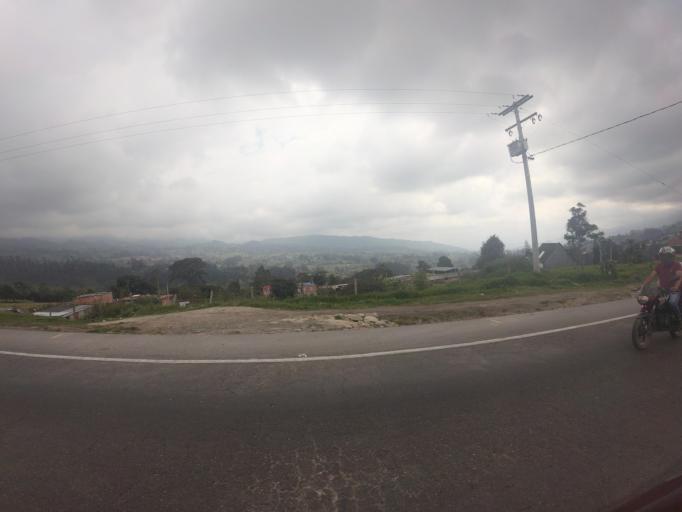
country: CO
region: Cundinamarca
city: San Antonio del Tequendama
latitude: 4.5243
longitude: -74.3524
